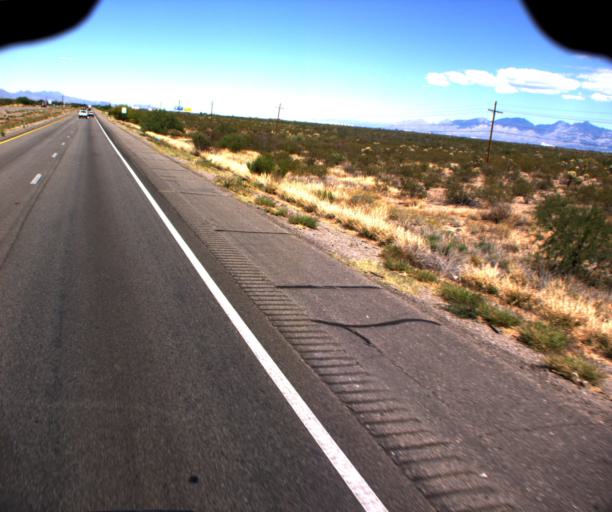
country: US
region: Arizona
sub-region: Pima County
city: Vail
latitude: 32.0661
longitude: -110.7806
